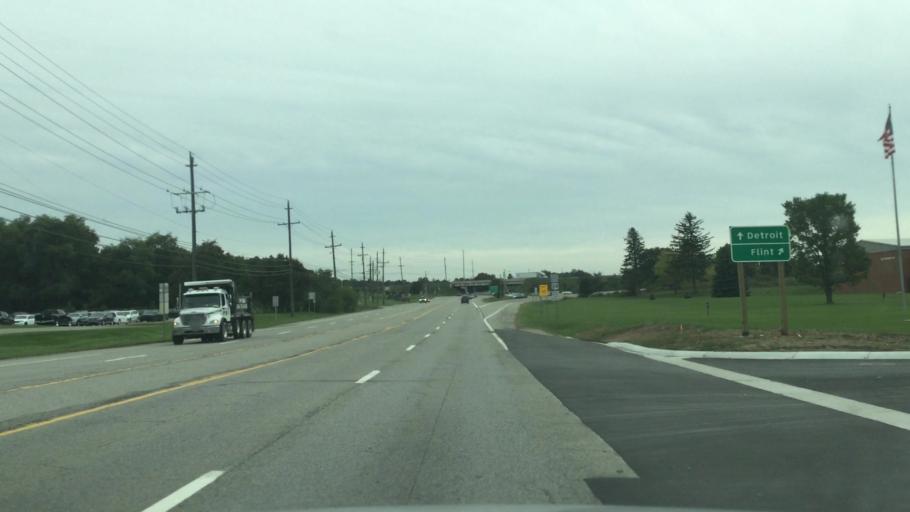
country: US
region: Michigan
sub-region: Oakland County
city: Clarkston
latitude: 42.7431
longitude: -83.4591
